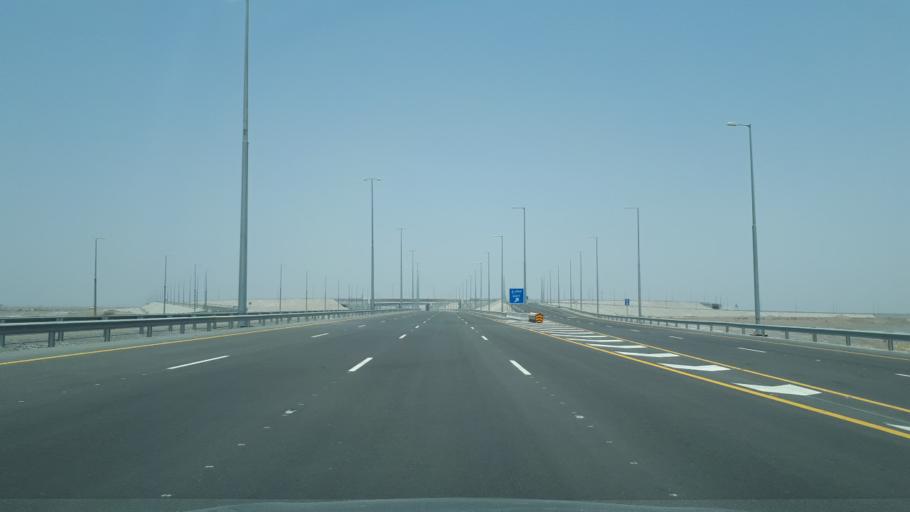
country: OM
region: Al Batinah
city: Barka'
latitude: 23.5761
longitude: 57.7440
